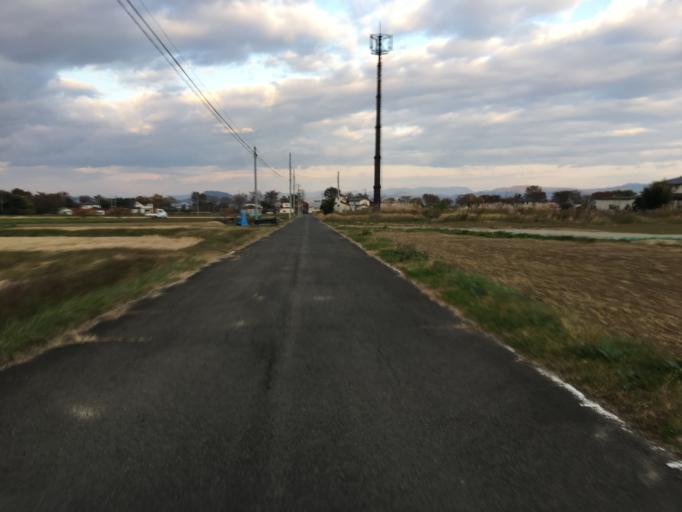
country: JP
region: Fukushima
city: Fukushima-shi
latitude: 37.7303
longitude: 140.3824
